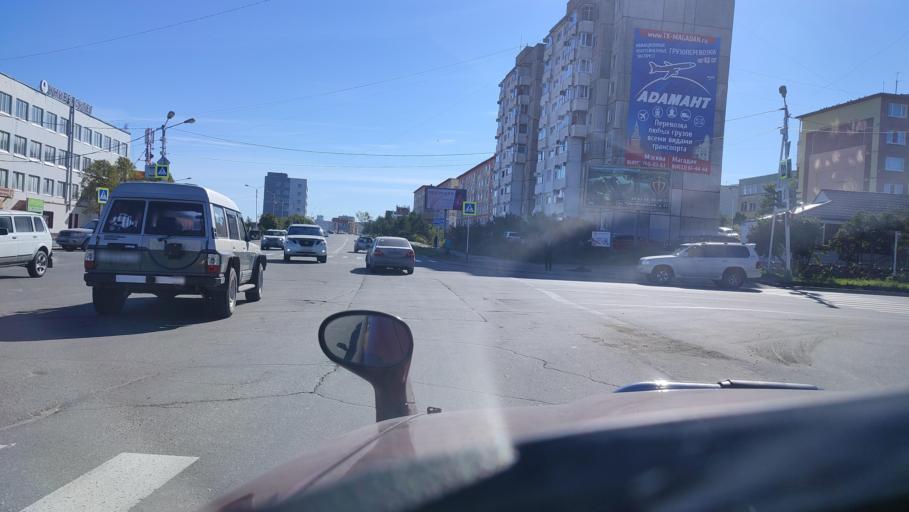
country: RU
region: Magadan
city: Magadan
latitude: 59.5612
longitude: 150.8183
